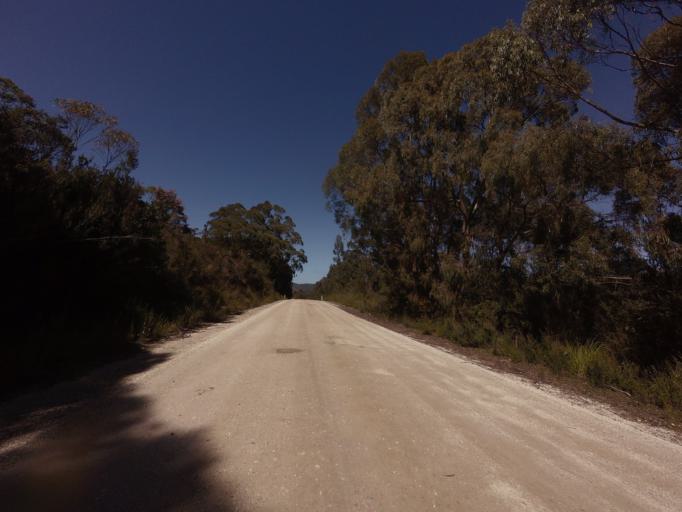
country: AU
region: Tasmania
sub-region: Huon Valley
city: Geeveston
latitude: -42.9395
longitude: 146.3482
